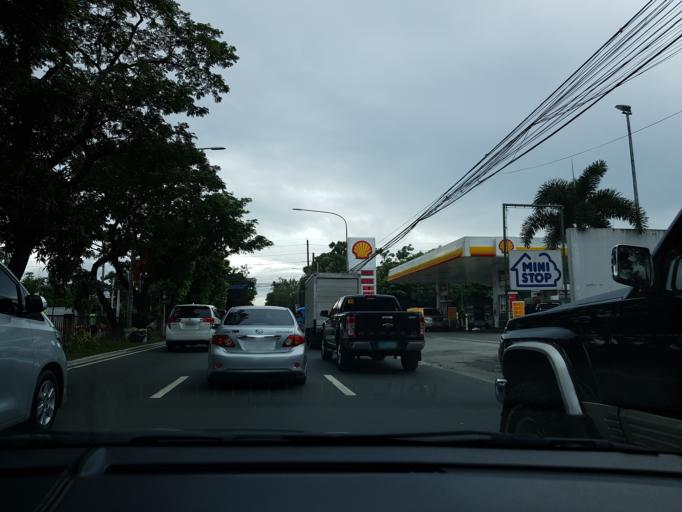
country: PH
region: Metro Manila
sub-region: San Juan
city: San Juan
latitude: 14.6001
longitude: 121.0491
